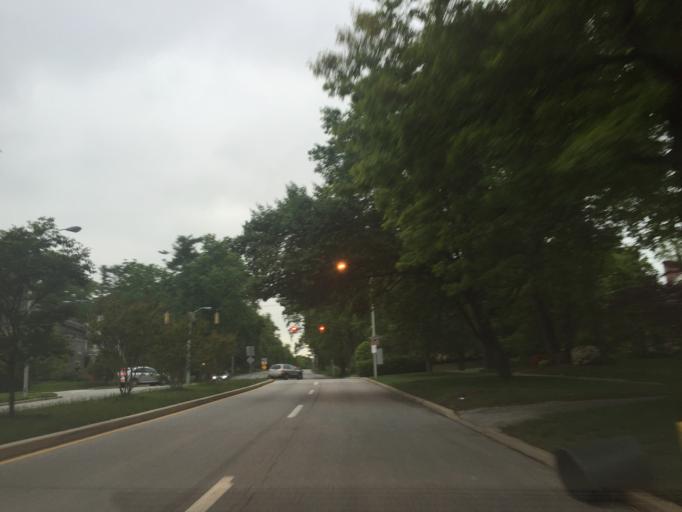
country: US
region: Maryland
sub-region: City of Baltimore
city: Baltimore
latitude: 39.3409
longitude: -76.6179
